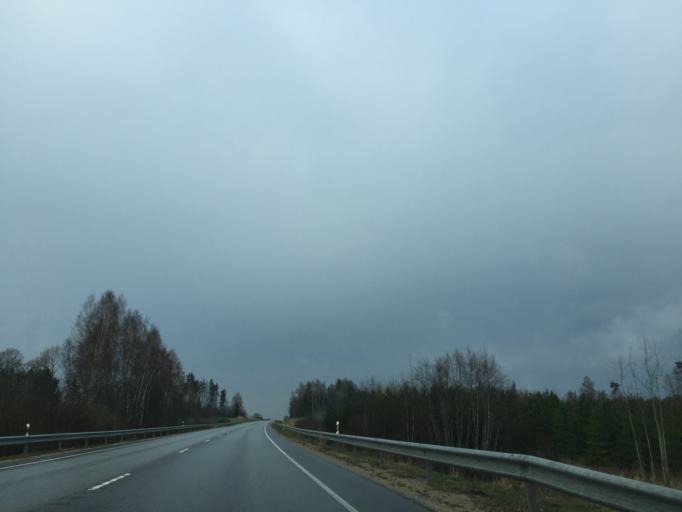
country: EE
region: Tartu
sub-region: UElenurme vald
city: Ulenurme
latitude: 58.1744
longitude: 26.6913
